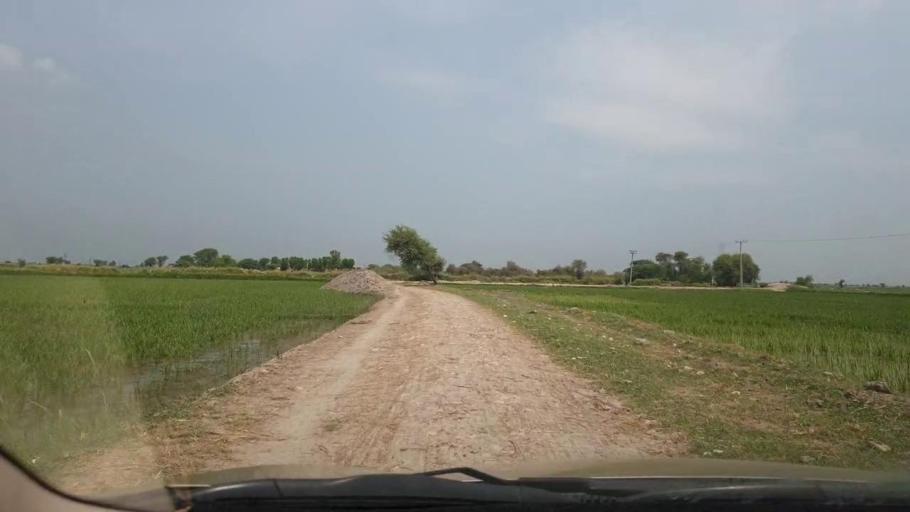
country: PK
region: Sindh
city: Goth Garelo
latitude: 27.5204
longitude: 68.1218
